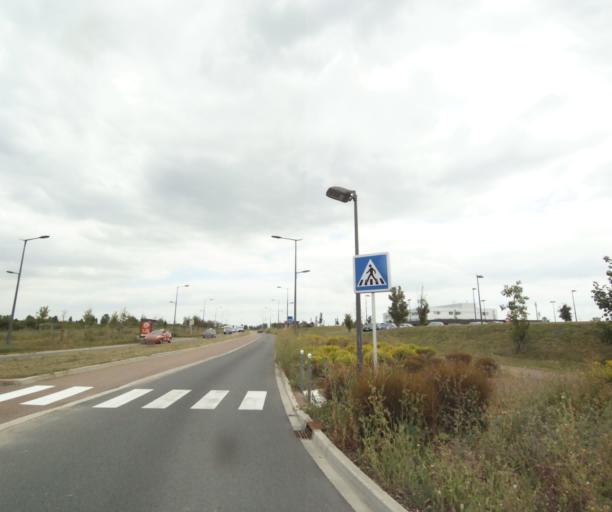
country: FR
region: Centre
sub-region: Departement du Loiret
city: Saran
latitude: 47.9403
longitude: 1.8807
